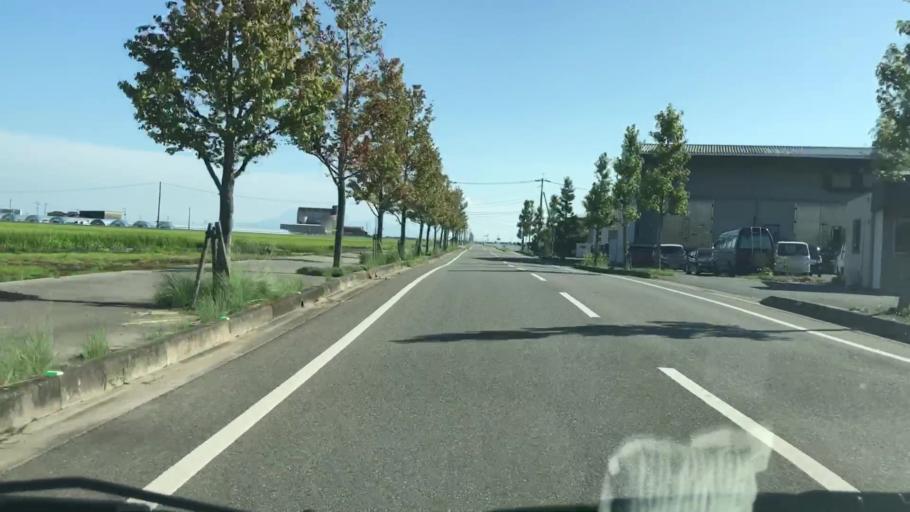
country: JP
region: Saga Prefecture
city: Okawa
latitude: 33.1800
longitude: 130.3130
